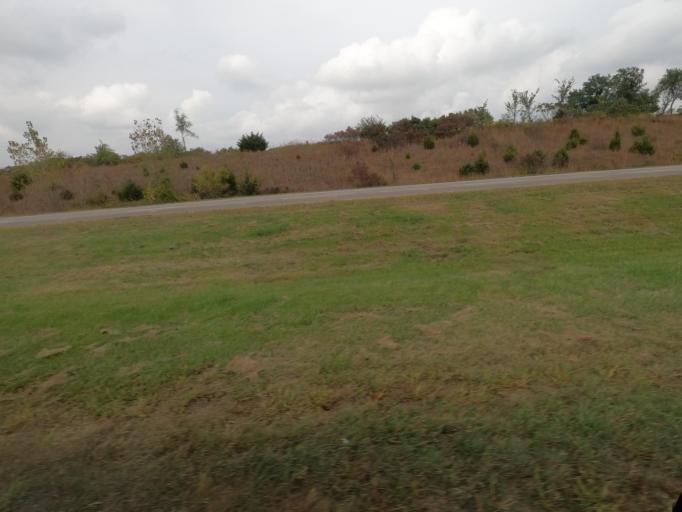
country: US
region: Iowa
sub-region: Wapello County
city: Ottumwa
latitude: 41.0962
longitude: -92.4895
